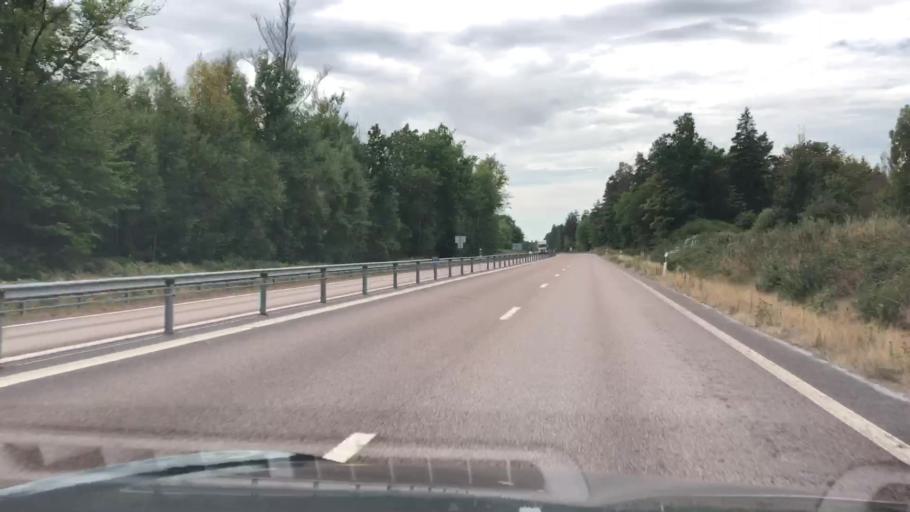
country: SE
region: Kalmar
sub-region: Torsas Kommun
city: Torsas
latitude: 56.2883
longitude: 15.9866
